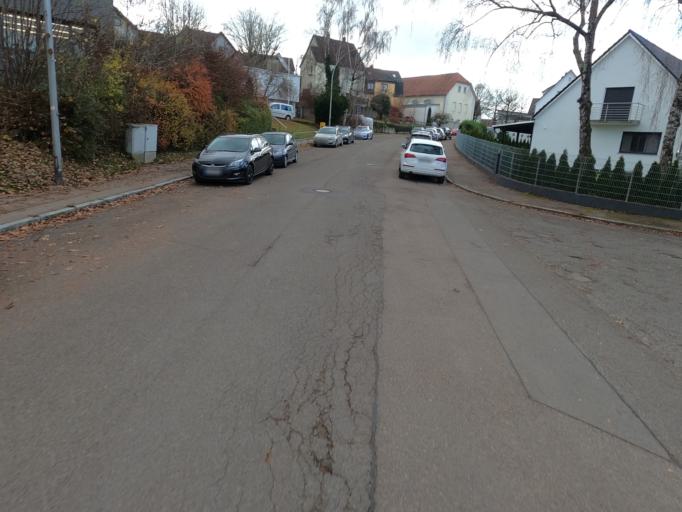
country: DE
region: Baden-Wuerttemberg
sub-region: Regierungsbezirk Stuttgart
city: Goeppingen
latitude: 48.6898
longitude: 9.6337
